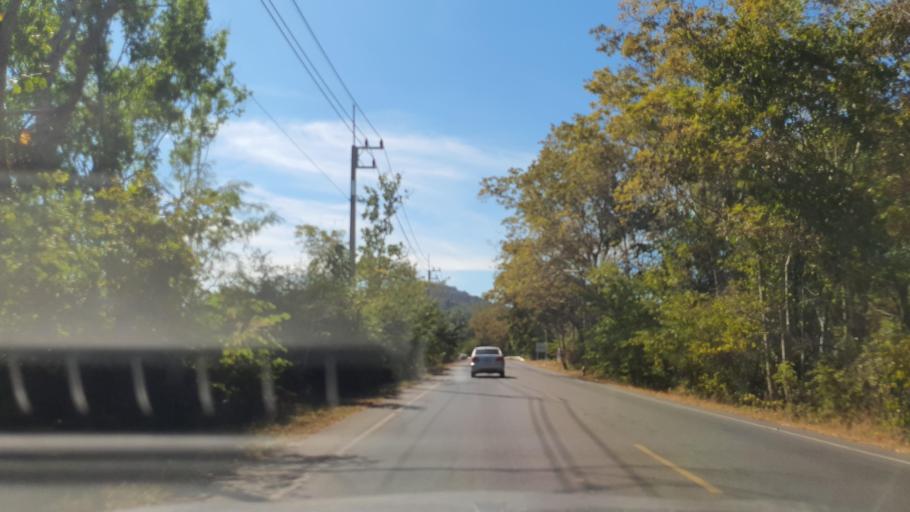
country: TH
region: Kalasin
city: Khao Wong
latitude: 16.7649
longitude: 104.1346
